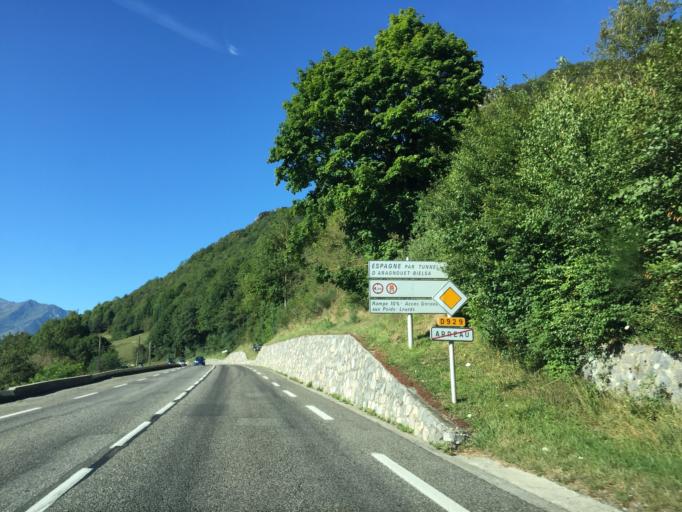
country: FR
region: Midi-Pyrenees
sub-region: Departement des Hautes-Pyrenees
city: Saint-Lary-Soulan
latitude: 42.9022
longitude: 0.3537
